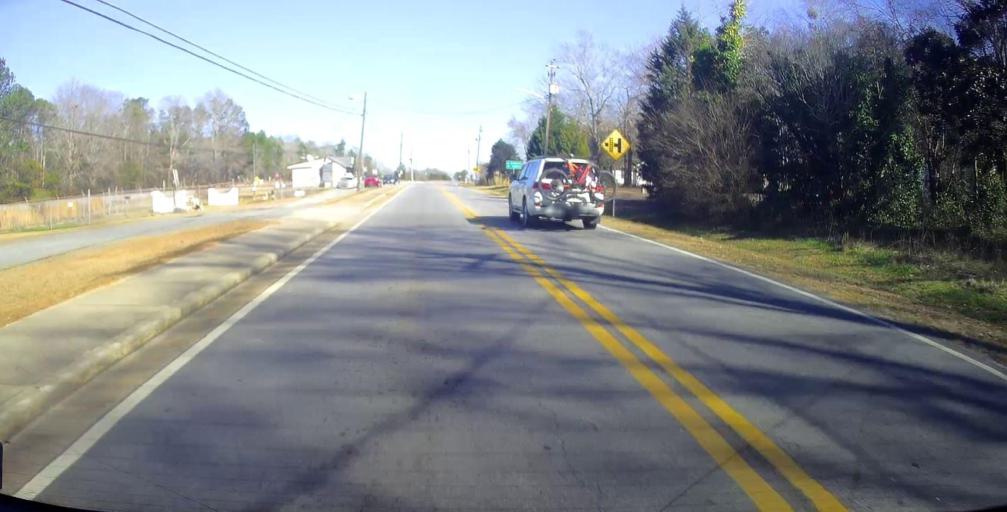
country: US
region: Georgia
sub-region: Taylor County
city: Butler
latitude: 32.5562
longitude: -84.2265
